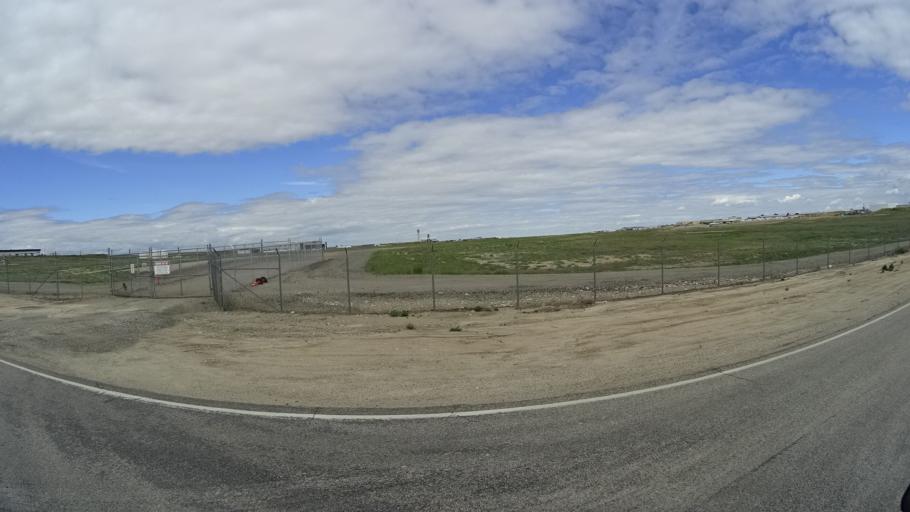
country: US
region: Idaho
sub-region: Ada County
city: Boise
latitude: 43.5520
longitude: -116.1872
